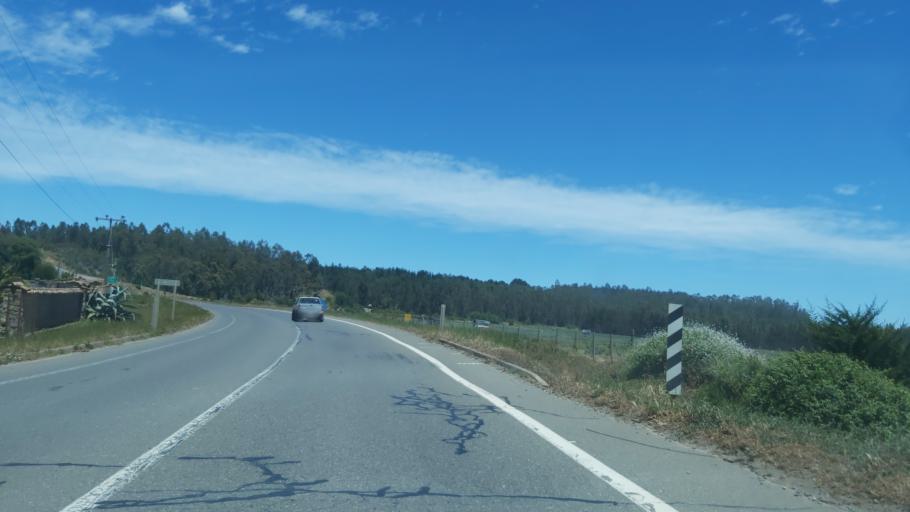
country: CL
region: Maule
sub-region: Provincia de Talca
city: Constitucion
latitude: -35.3129
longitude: -72.3837
